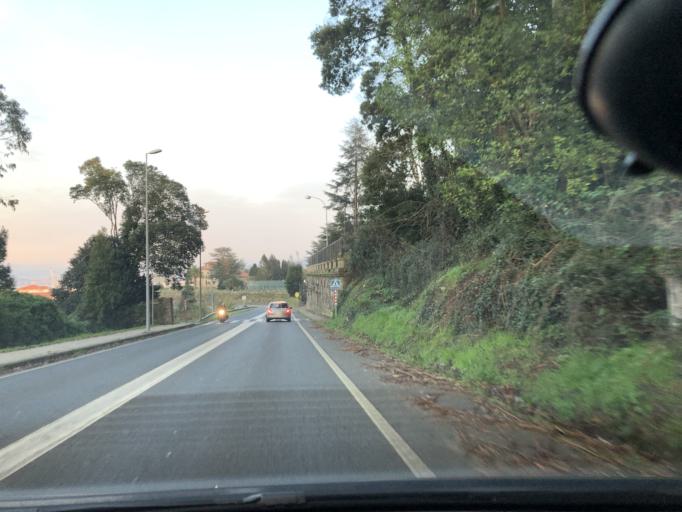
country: ES
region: Galicia
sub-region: Provincia de Pontevedra
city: Marin
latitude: 42.3919
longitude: -8.7121
